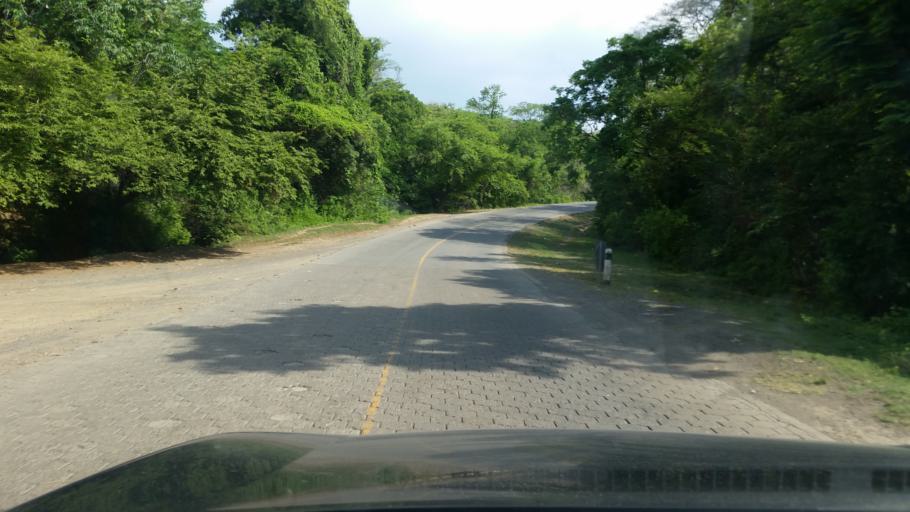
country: NI
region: Managua
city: Carlos Fonseca Amador
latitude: 11.9021
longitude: -86.5106
